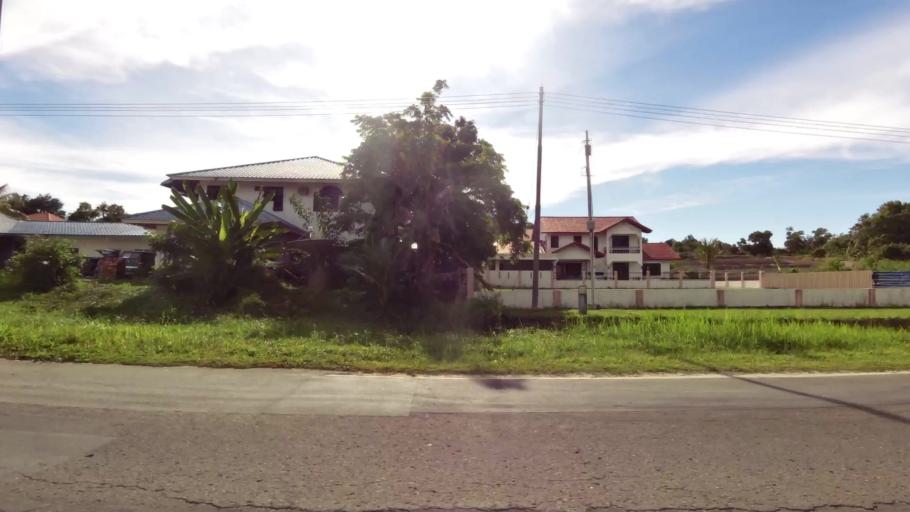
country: BN
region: Brunei and Muara
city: Bandar Seri Begawan
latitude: 4.9809
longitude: 115.0215
